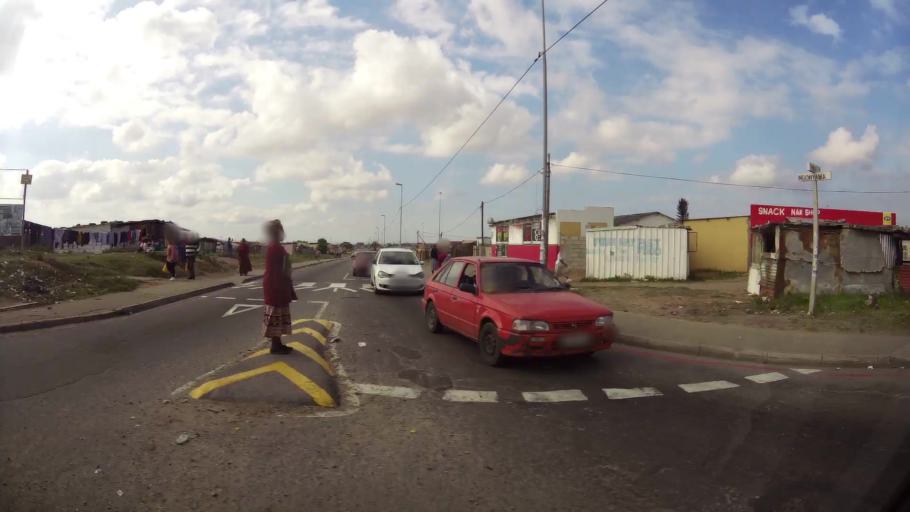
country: ZA
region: Eastern Cape
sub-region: Nelson Mandela Bay Metropolitan Municipality
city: Port Elizabeth
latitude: -33.8021
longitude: 25.5869
